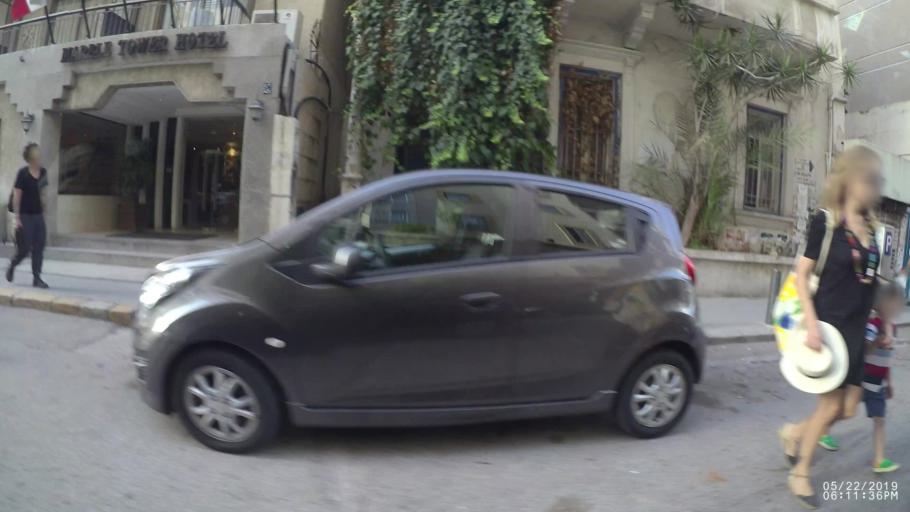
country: LB
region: Beyrouth
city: Ra's Bayrut
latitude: 33.8967
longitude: 35.4809
